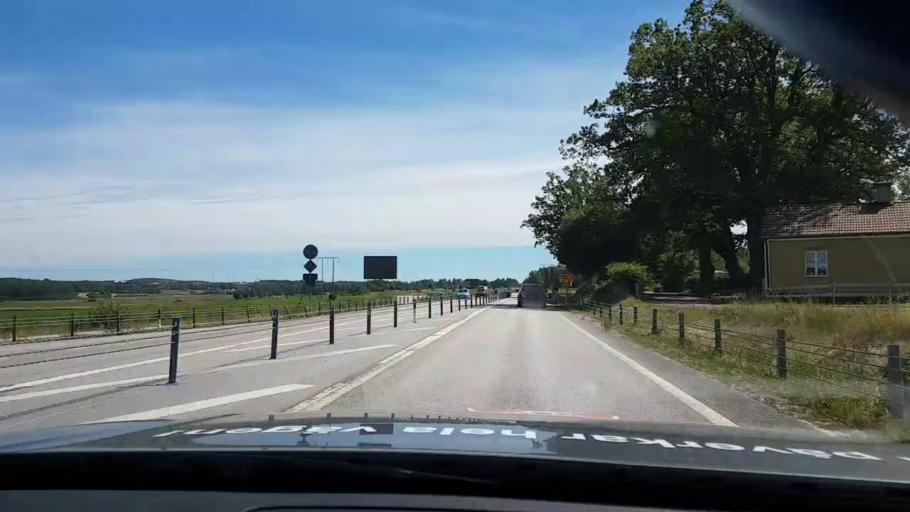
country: SE
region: Kalmar
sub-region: Vasterviks Kommun
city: Vaestervik
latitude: 57.7773
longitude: 16.5406
